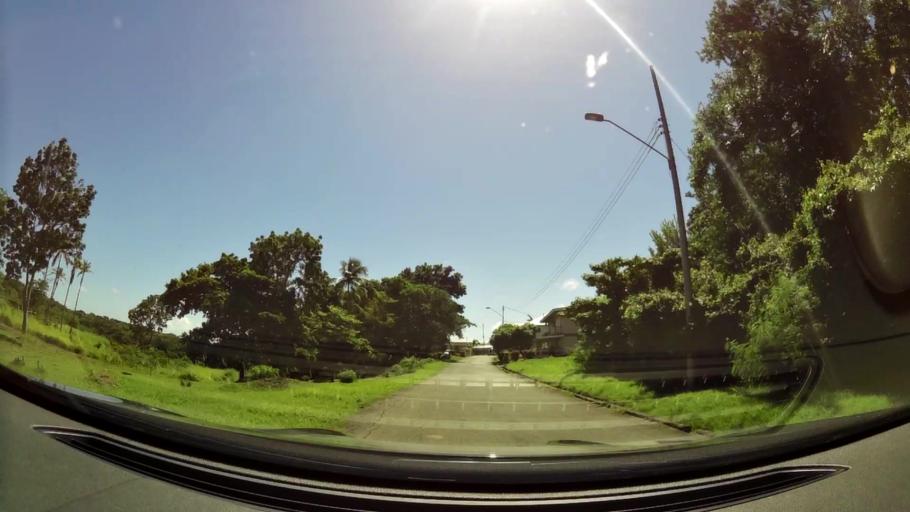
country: TT
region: Tobago
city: Scarborough
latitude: 11.1751
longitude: -60.7792
